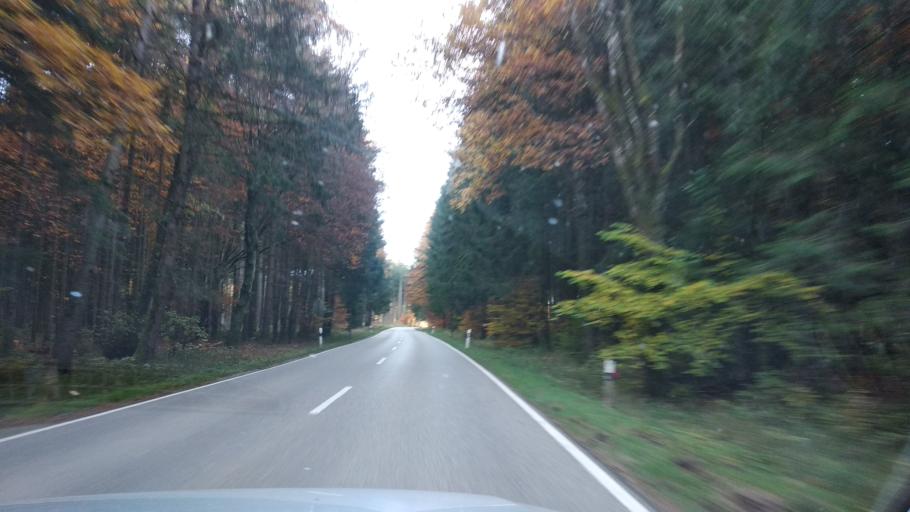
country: DE
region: Bavaria
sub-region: Upper Bavaria
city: Zorneding
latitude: 48.0705
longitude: 11.8369
